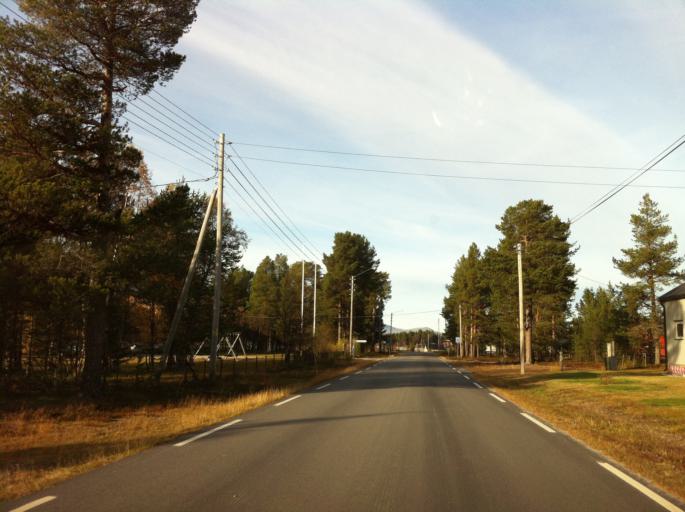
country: NO
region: Hedmark
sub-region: Engerdal
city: Engerdal
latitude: 62.1544
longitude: 11.9485
